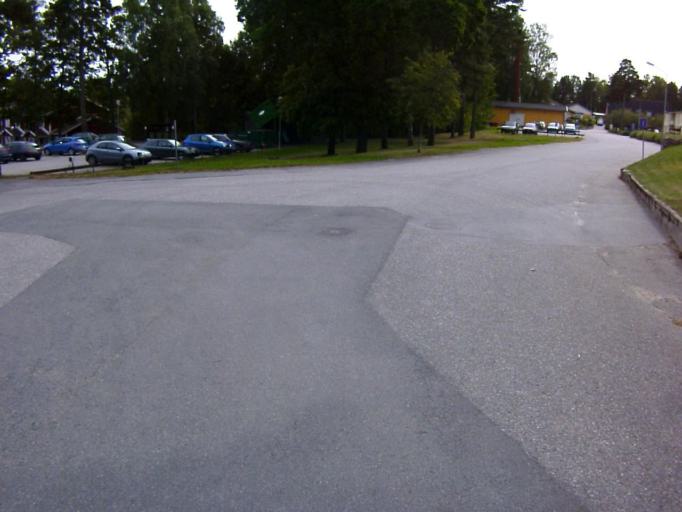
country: SE
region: Soedermanland
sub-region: Eskilstuna Kommun
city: Arla
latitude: 59.3872
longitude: 16.6760
